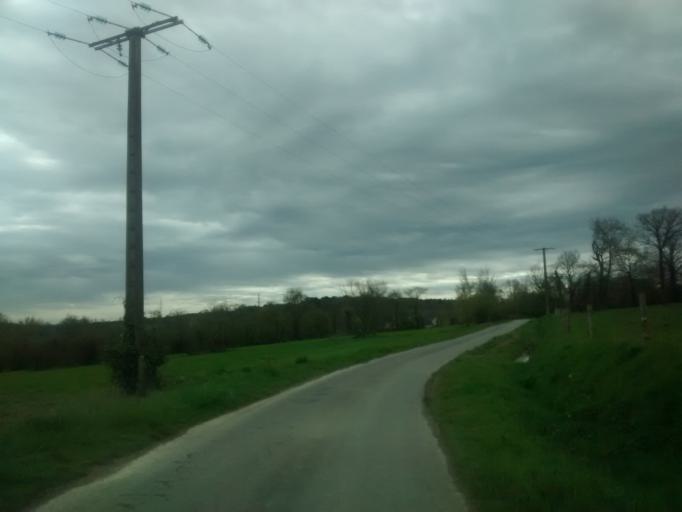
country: FR
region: Brittany
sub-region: Departement d'Ille-et-Vilaine
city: Erce-pres-Liffre
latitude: 48.2412
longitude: -1.4997
